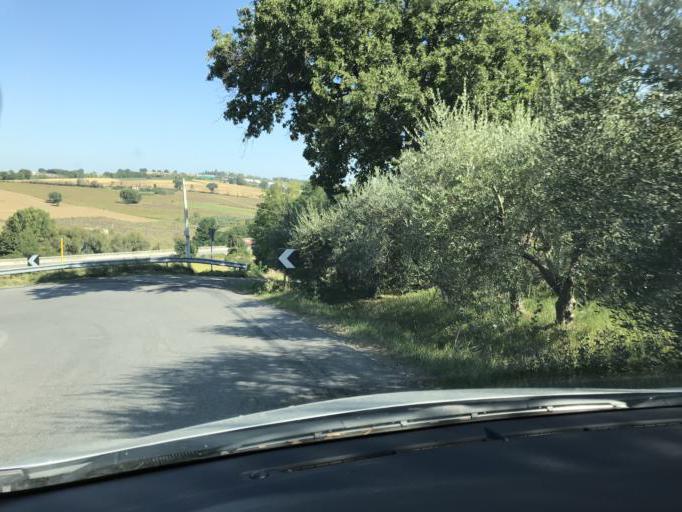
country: IT
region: Umbria
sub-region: Provincia di Perugia
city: Via Lippia
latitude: 43.1043
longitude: 12.4877
